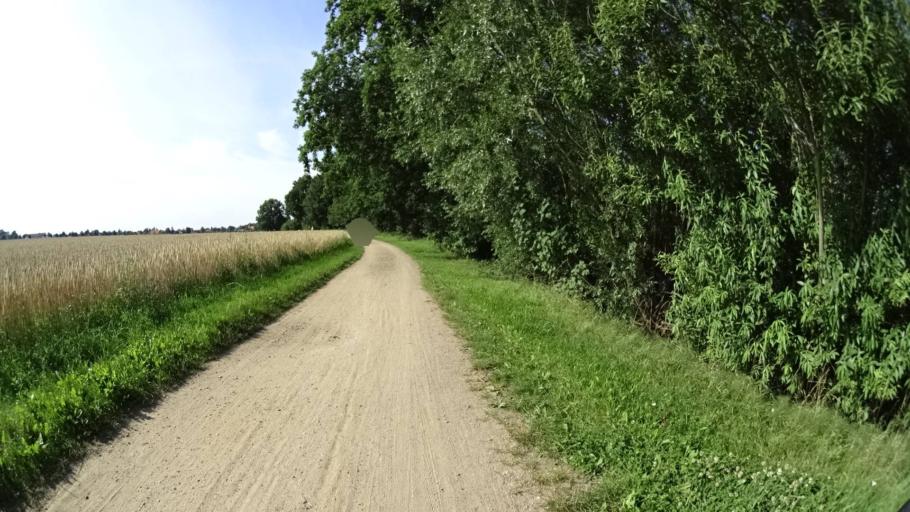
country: DE
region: Lower Saxony
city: Bardowick
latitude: 53.2838
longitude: 10.4051
